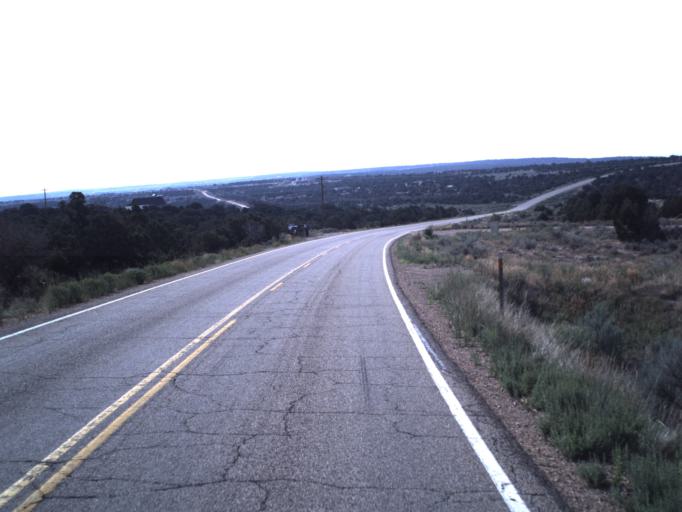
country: US
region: Utah
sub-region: Duchesne County
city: Duchesne
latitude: 40.3122
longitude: -110.3788
